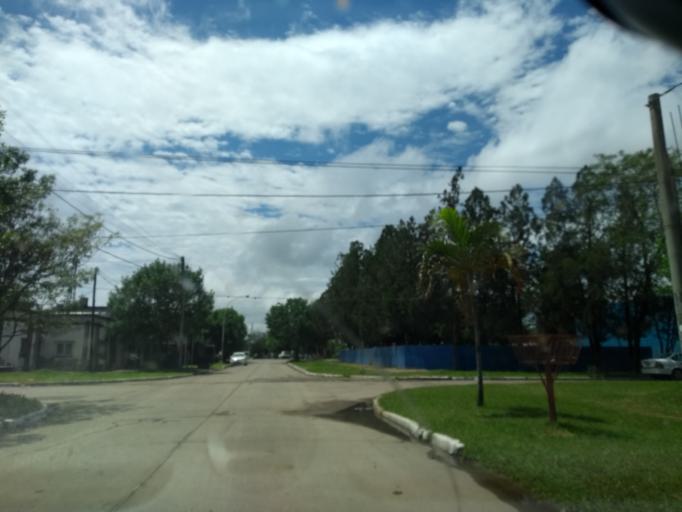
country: AR
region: Chaco
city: Barranqueras
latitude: -27.4823
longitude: -58.9445
